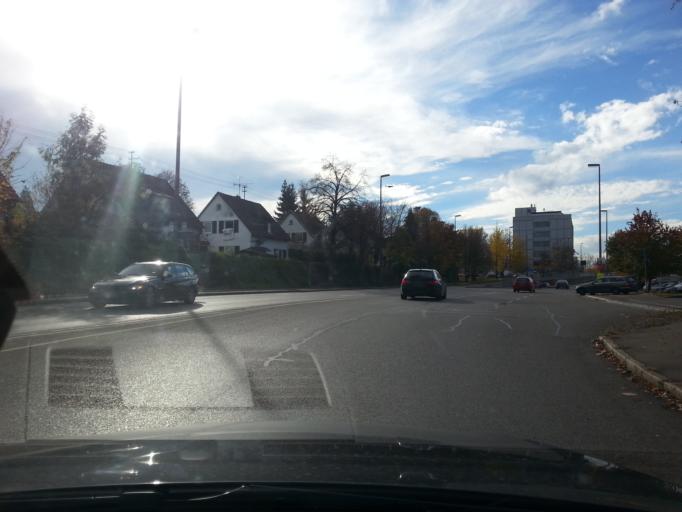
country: DE
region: Baden-Wuerttemberg
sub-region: Regierungsbezirk Stuttgart
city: Sindelfingen
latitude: 48.7010
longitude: 9.0082
